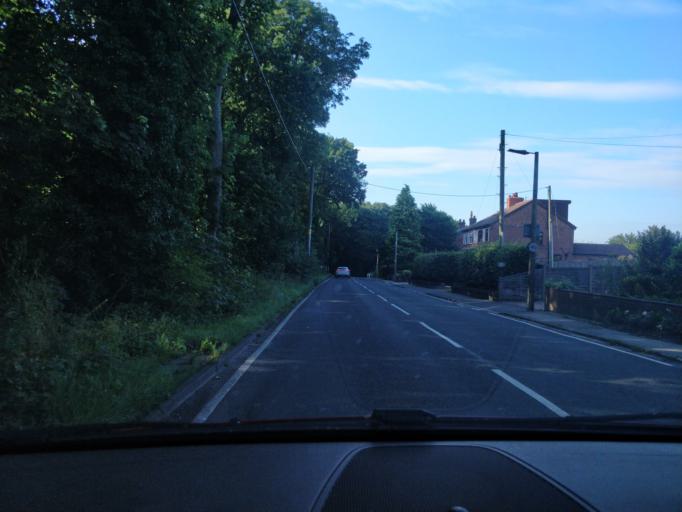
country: GB
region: England
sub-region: Lancashire
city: Banks
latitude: 53.6542
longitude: -2.8781
